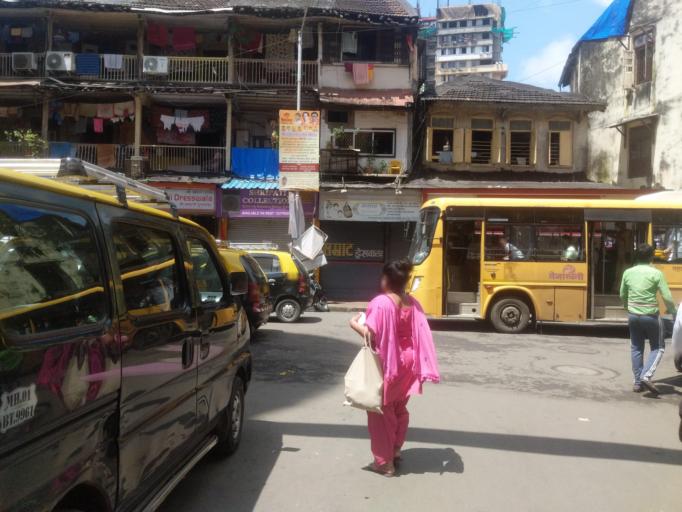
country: IN
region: Maharashtra
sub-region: Mumbai Suburban
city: Mumbai
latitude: 18.9530
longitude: 72.8253
